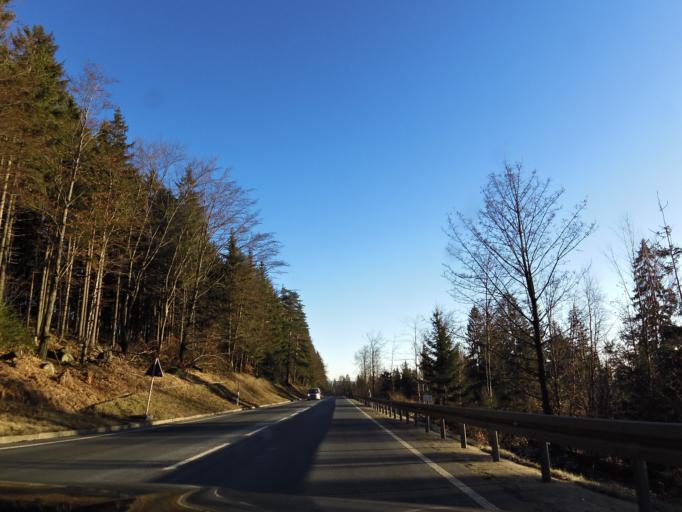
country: DE
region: Bavaria
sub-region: Upper Franconia
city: Fichtelberg
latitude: 50.0097
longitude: 11.8851
